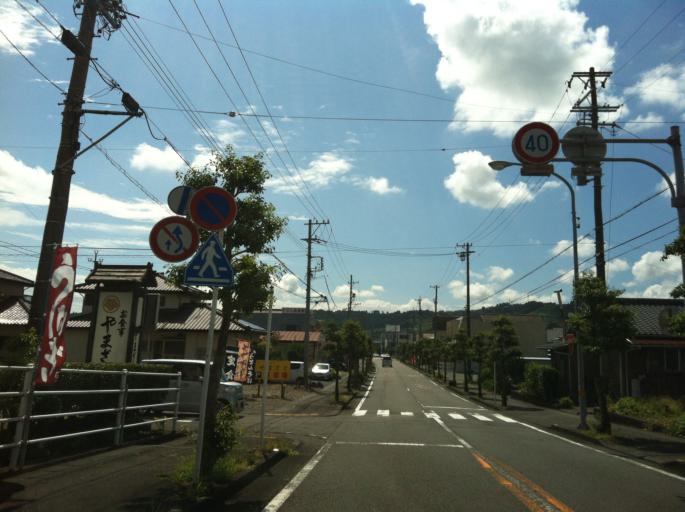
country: JP
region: Shizuoka
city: Kanaya
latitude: 34.8327
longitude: 138.1270
